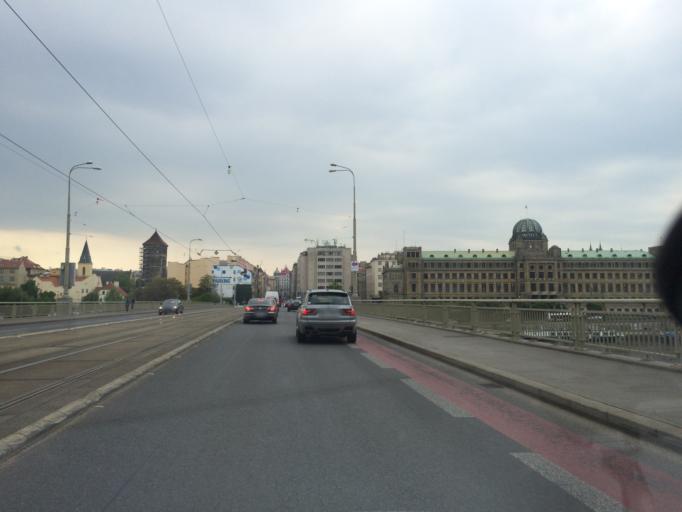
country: CZ
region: Praha
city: Prague
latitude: 50.0951
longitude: 14.4267
